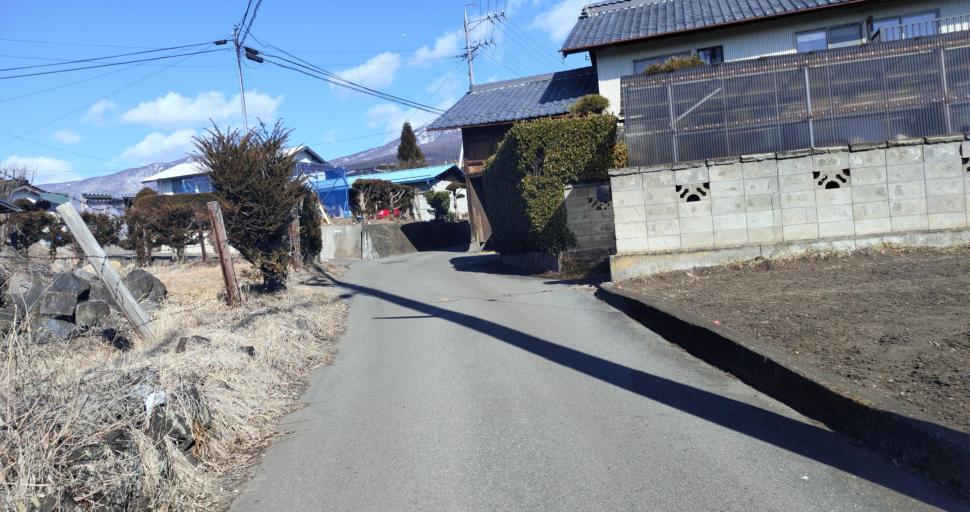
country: JP
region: Nagano
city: Komoro
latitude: 36.3362
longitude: 138.4935
